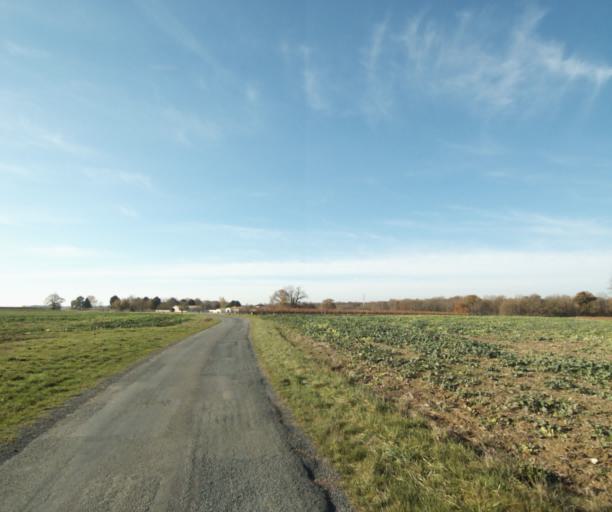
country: FR
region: Poitou-Charentes
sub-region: Departement de la Charente-Maritime
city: Chaniers
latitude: 45.7549
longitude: -0.5141
